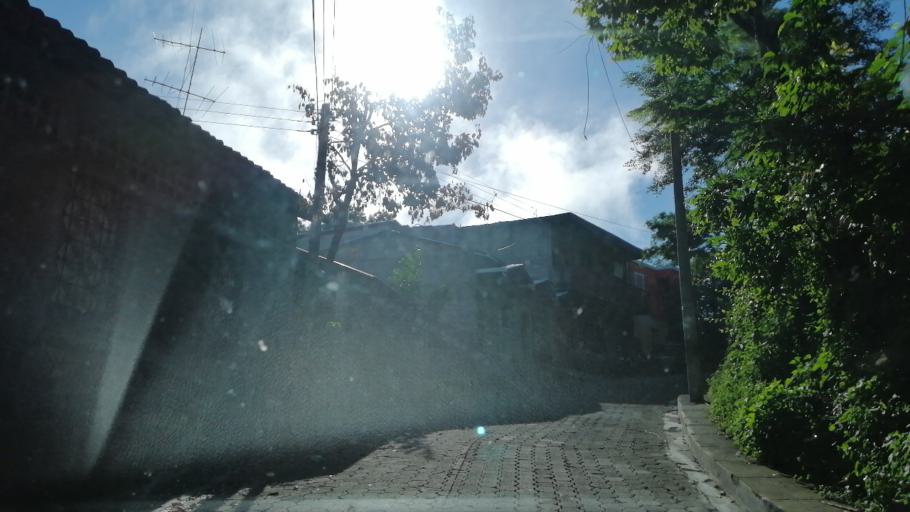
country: SV
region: Morazan
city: Cacaopera
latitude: 13.7756
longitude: -88.0834
